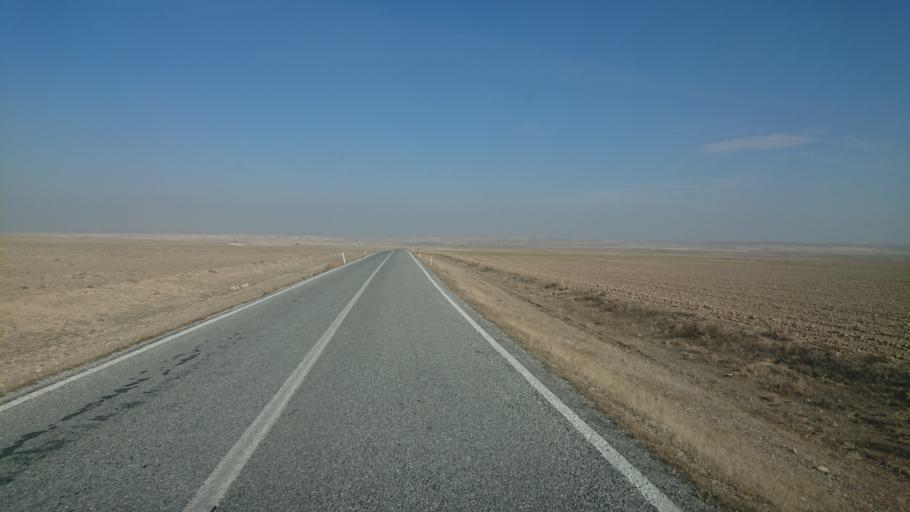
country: TR
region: Aksaray
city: Sultanhani
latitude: 38.0344
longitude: 33.5775
